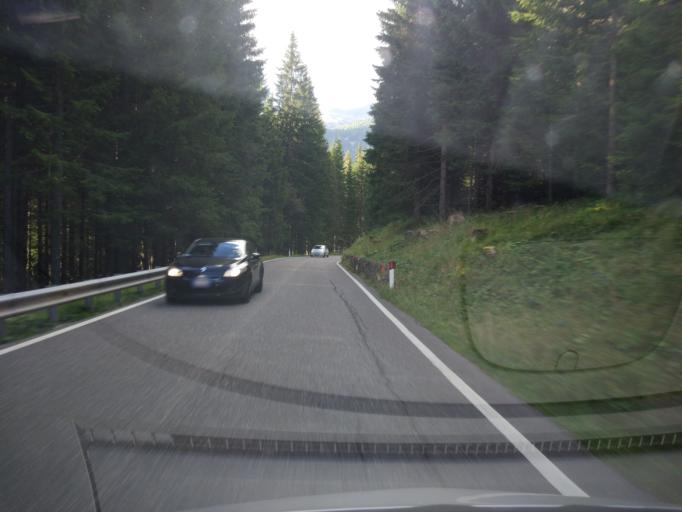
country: IT
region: Veneto
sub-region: Provincia di Belluno
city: Falcade Alto
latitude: 46.3035
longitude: 11.7601
